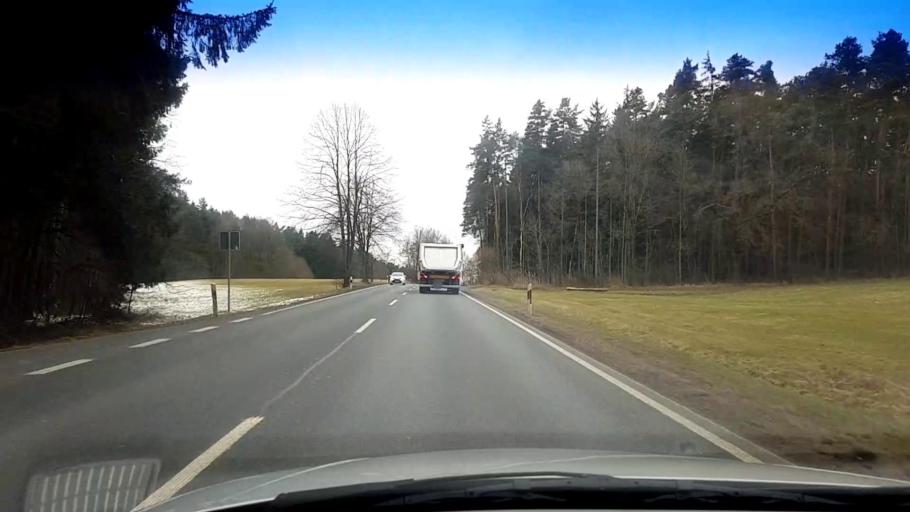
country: DE
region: Bavaria
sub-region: Upper Franconia
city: Neudrossenfeld
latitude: 50.0433
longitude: 11.4863
